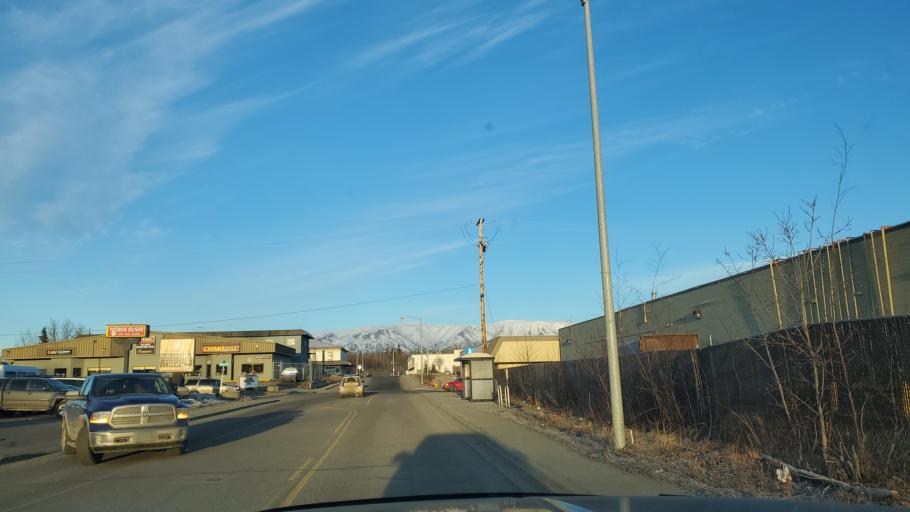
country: US
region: Alaska
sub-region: Matanuska-Susitna Borough
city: Wasilla
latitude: 61.5817
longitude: -149.4372
